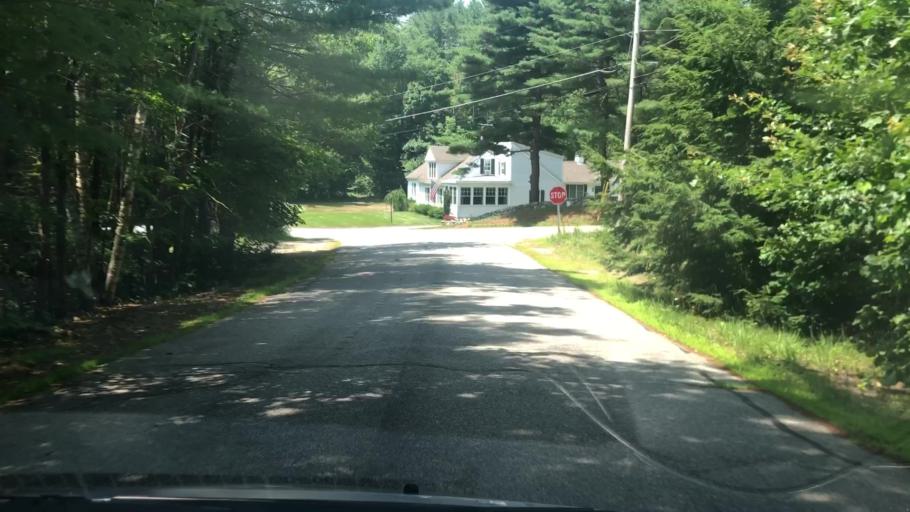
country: US
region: New Hampshire
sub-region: Hillsborough County
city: Milford
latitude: 42.8720
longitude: -71.6226
